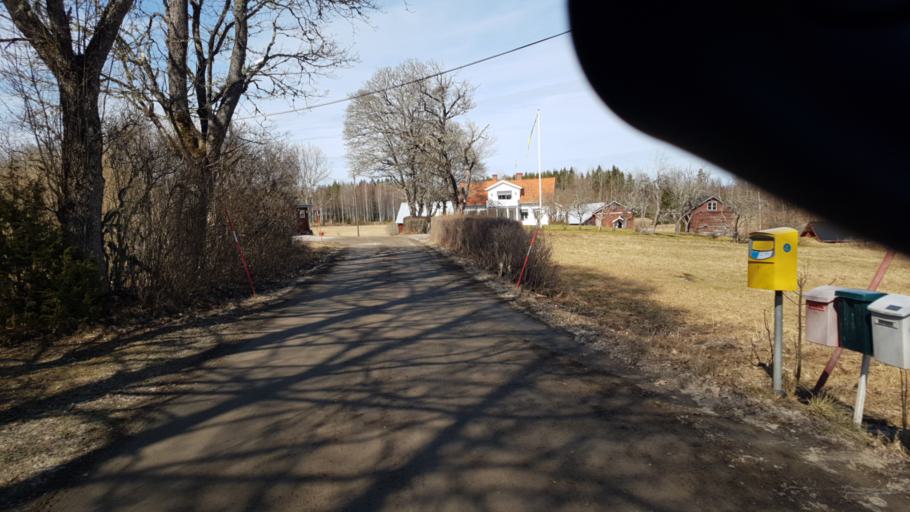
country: SE
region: Vaermland
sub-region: Arvika Kommun
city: Arvika
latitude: 59.5513
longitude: 12.8501
